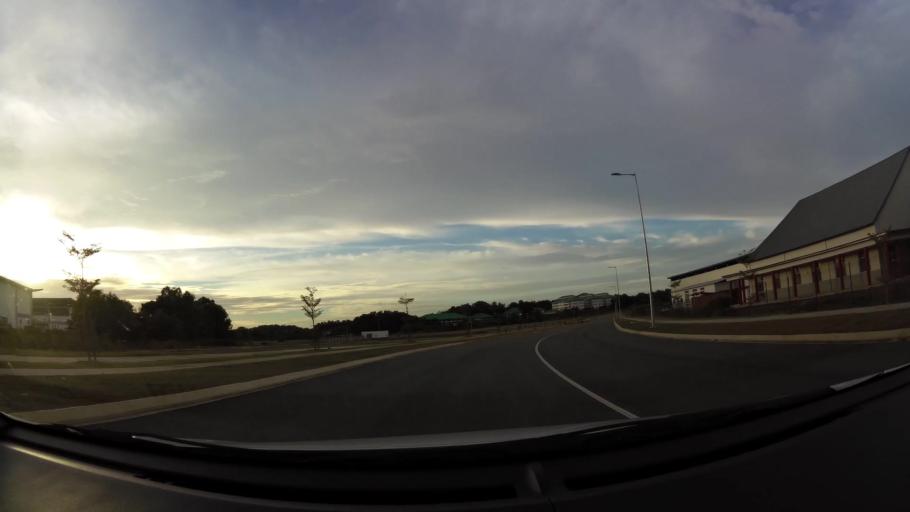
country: BN
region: Brunei and Muara
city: Bandar Seri Begawan
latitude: 4.9874
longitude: 114.9831
